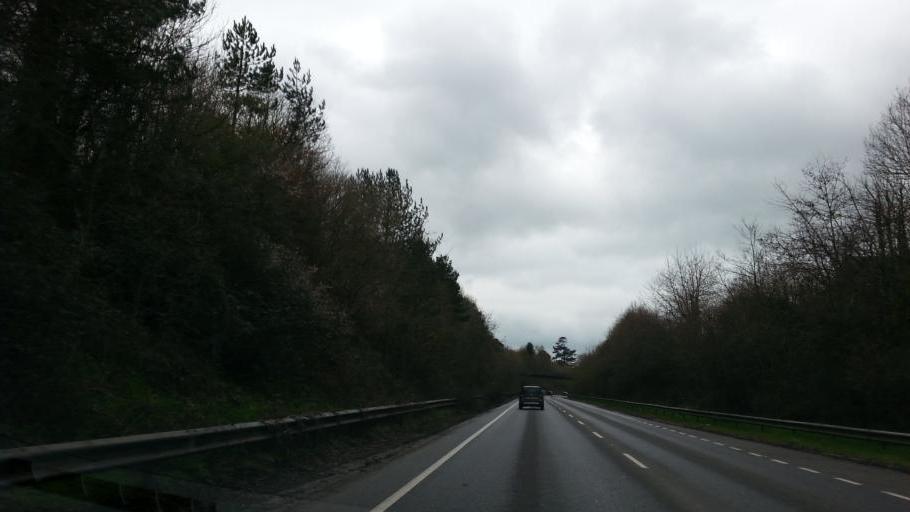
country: GB
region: England
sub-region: Devon
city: Barnstaple
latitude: 51.0682
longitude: -4.0363
